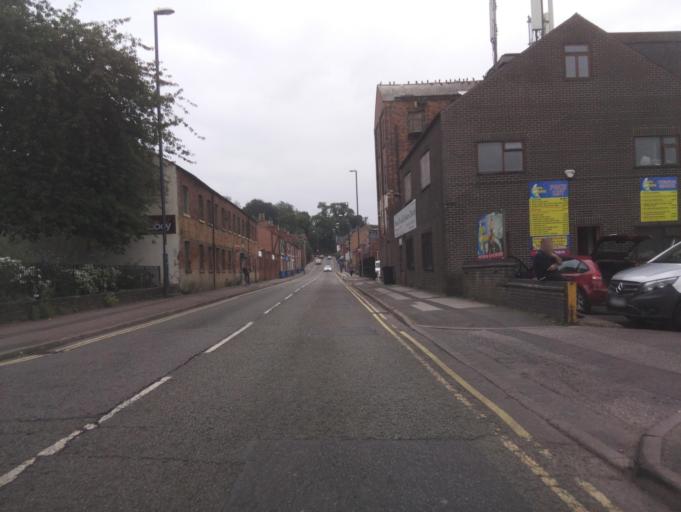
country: GB
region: England
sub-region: Derby
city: Derby
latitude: 52.9162
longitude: -1.4834
